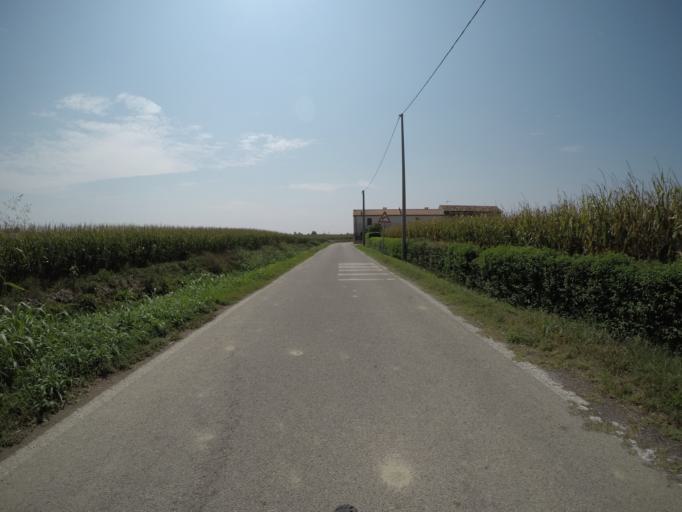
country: IT
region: Veneto
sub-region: Provincia di Rovigo
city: Lendinara
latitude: 45.0986
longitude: 11.5892
